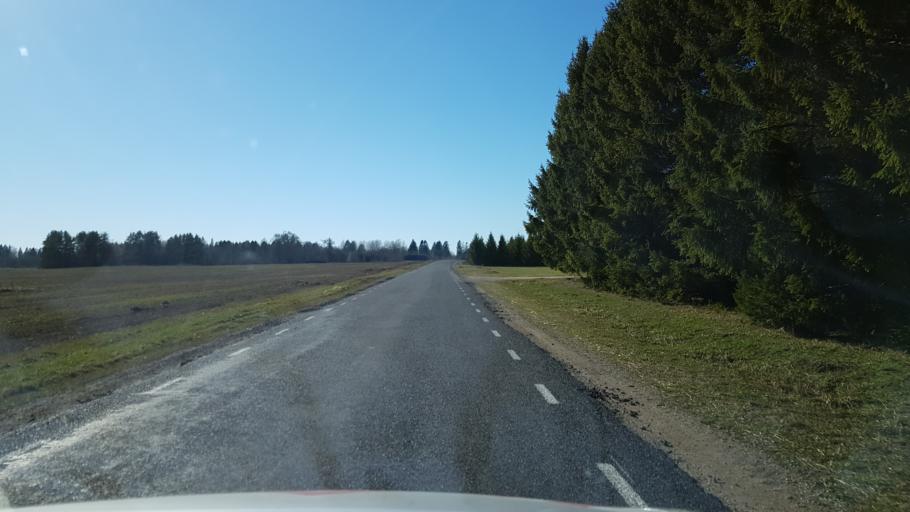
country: EE
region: Laeaene-Virumaa
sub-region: Haljala vald
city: Haljala
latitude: 59.4399
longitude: 26.1648
